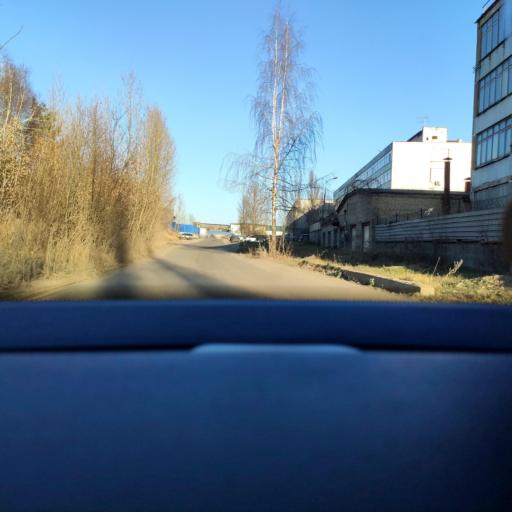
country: RU
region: Moskovskaya
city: Kotel'niki
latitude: 55.6321
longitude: 37.8232
